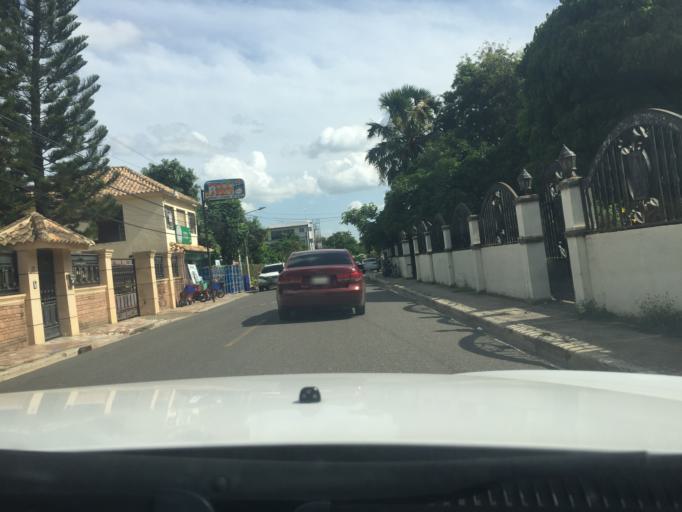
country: DO
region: Santiago
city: Tamboril
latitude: 19.4820
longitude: -70.6554
